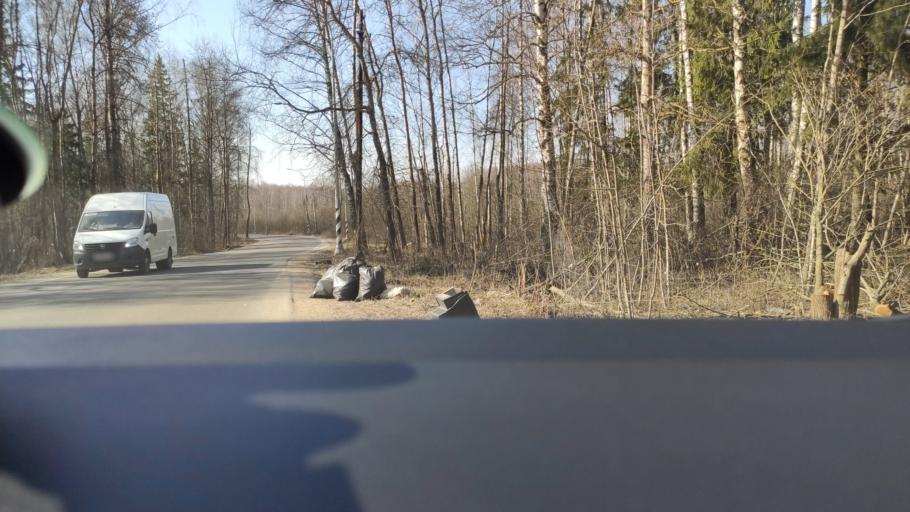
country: RU
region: Moskovskaya
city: Elektrostal'
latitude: 55.7724
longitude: 38.4124
